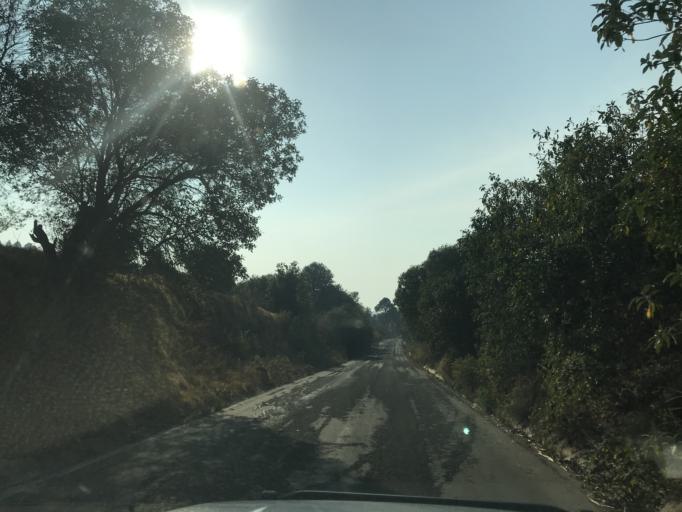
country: MX
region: Puebla
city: San Nicolas de los Ranchos
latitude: 19.0869
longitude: -98.5302
